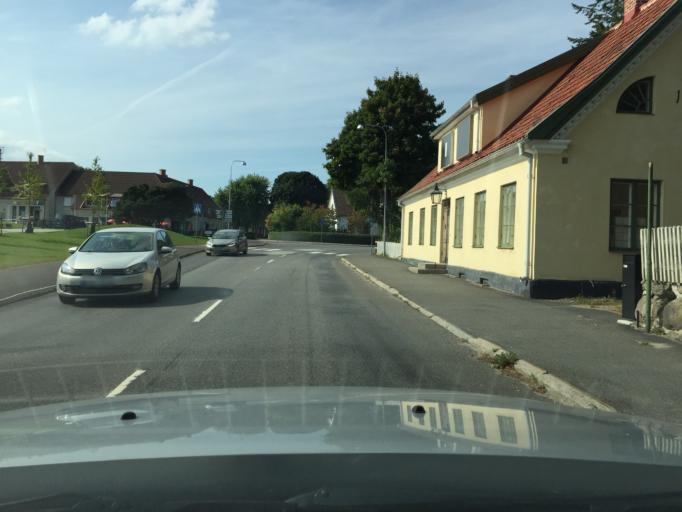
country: SE
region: Skane
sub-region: Kristianstads Kommun
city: Degeberga
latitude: 55.7256
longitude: 14.1015
